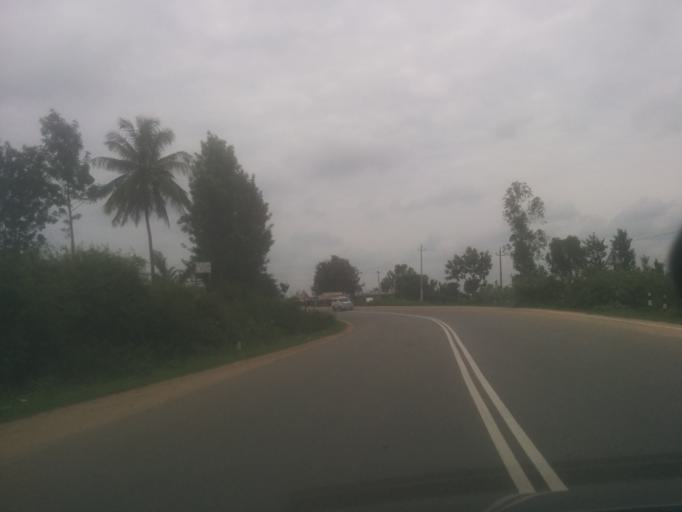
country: IN
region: Karnataka
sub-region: Hassan
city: Belur
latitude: 13.1649
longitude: 75.8819
